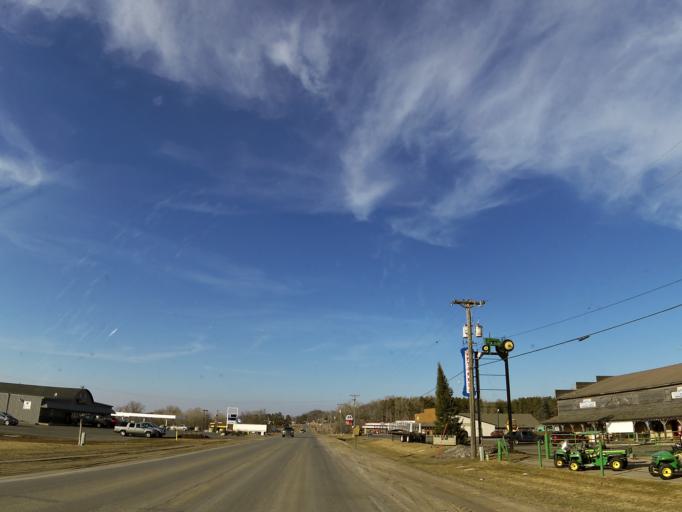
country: US
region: Minnesota
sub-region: Goodhue County
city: Cannon Falls
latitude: 44.4892
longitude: -92.9067
